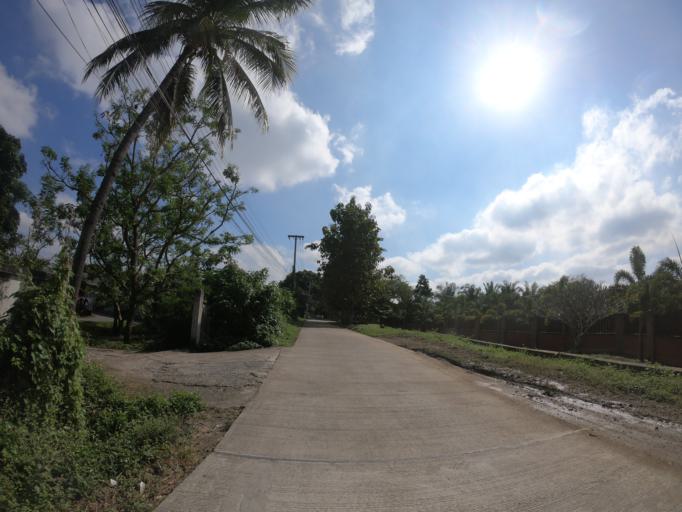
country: TH
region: Chiang Mai
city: Saraphi
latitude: 18.7154
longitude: 99.0201
